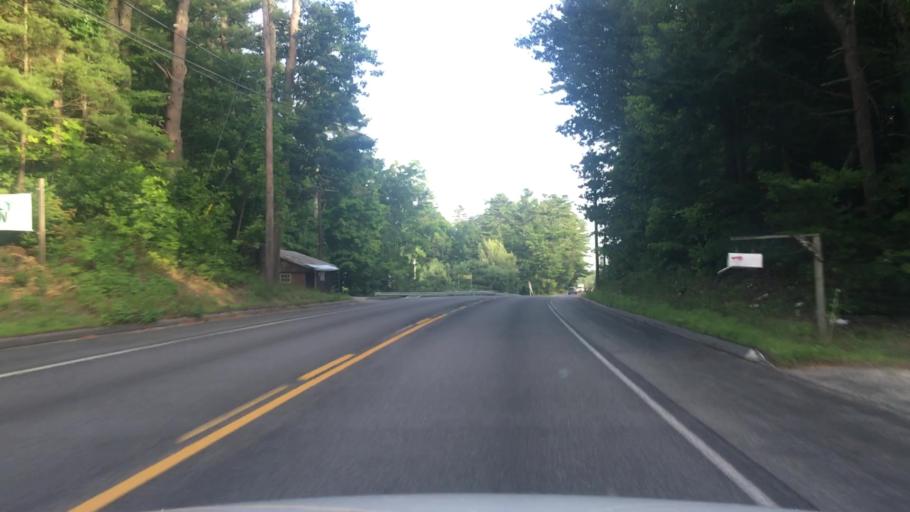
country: US
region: Maine
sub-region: Cumberland County
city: North Windham
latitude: 43.7940
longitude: -70.3989
